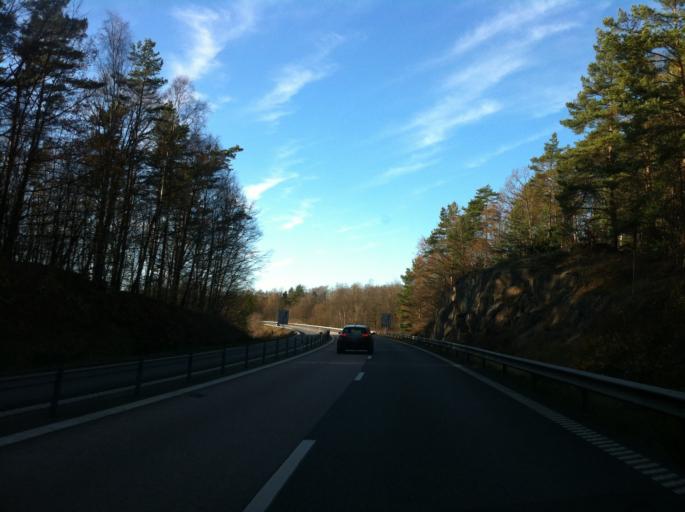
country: SE
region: Blekinge
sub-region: Karlshamns Kommun
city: Karlshamn
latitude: 56.1897
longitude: 14.8993
